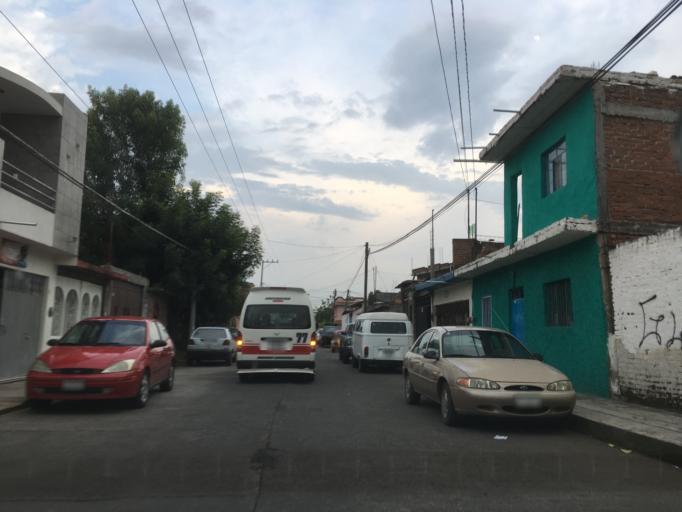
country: MX
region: Michoacan
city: Morelia
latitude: 19.6932
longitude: -101.2274
